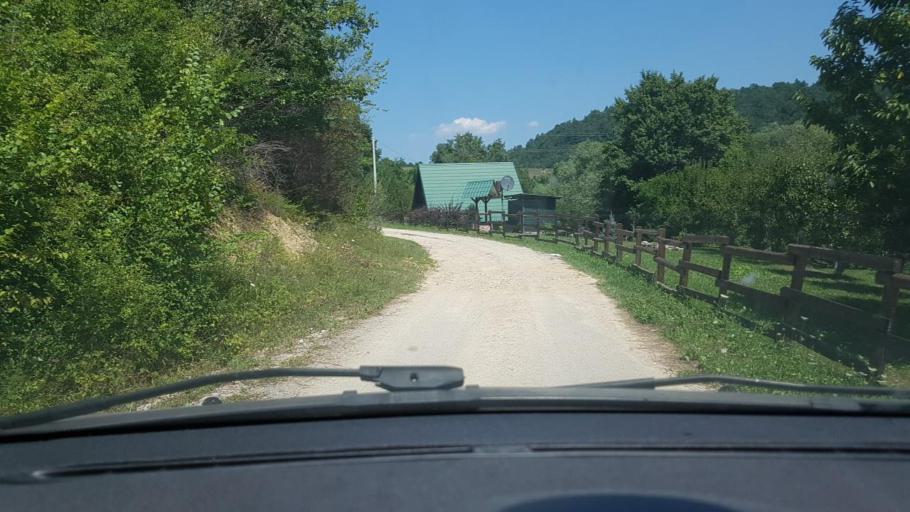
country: BA
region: Federation of Bosnia and Herzegovina
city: Orasac
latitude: 44.5649
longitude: 16.0801
